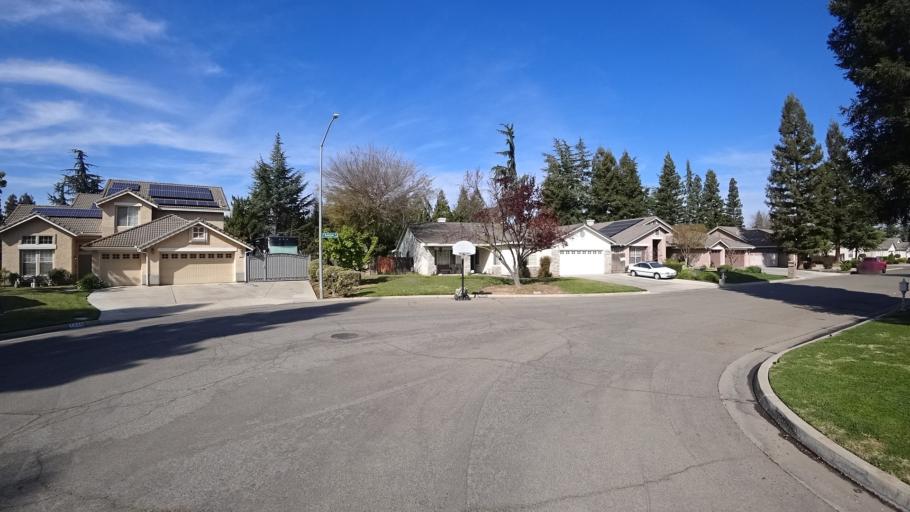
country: US
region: California
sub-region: Fresno County
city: West Park
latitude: 36.8412
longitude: -119.8784
